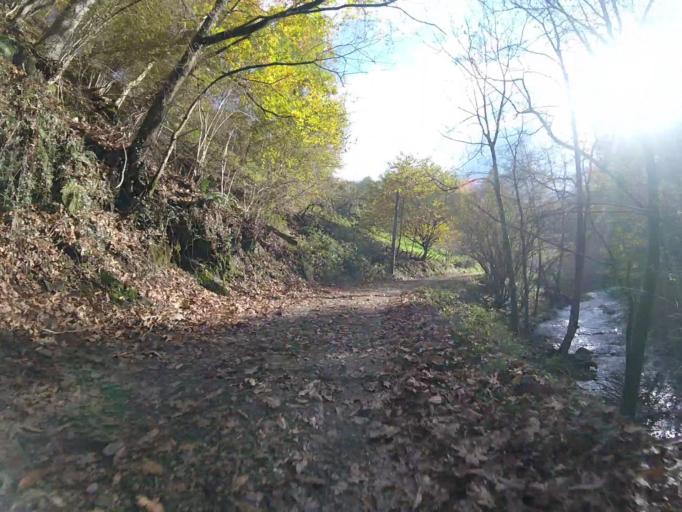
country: ES
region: Navarre
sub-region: Provincia de Navarra
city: Arantza
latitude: 43.2135
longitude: -1.7994
